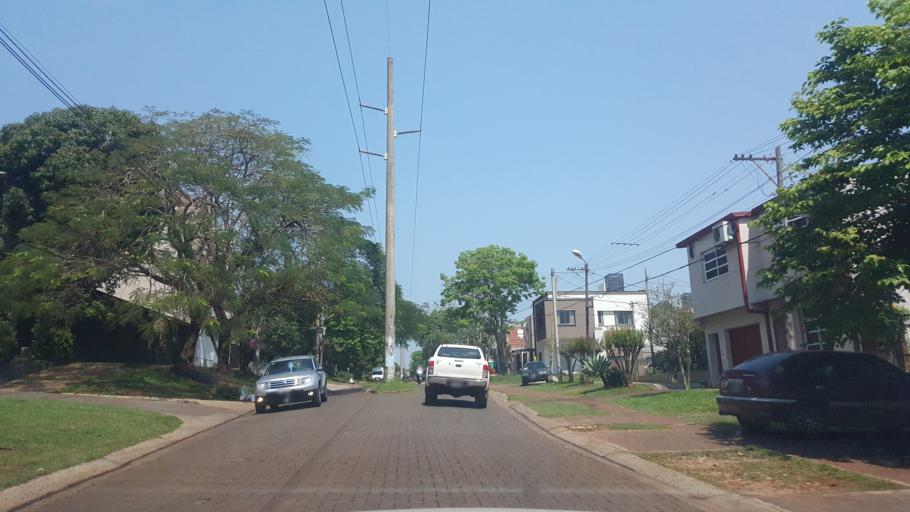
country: AR
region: Misiones
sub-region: Departamento de Capital
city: Posadas
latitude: -27.3741
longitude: -55.9137
